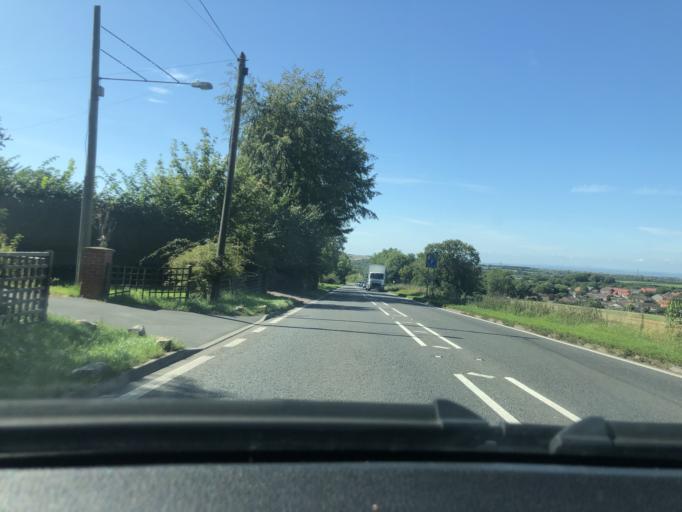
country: GB
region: England
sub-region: Somerset
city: Puriton
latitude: 51.1645
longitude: -2.9725
